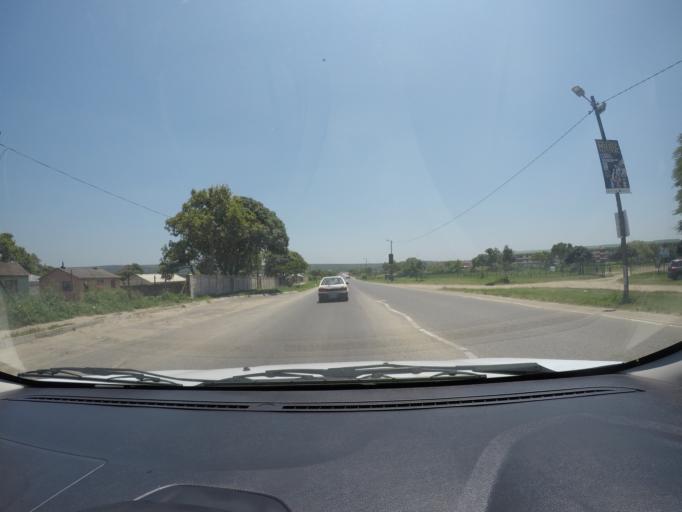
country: ZA
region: KwaZulu-Natal
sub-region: uThungulu District Municipality
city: eSikhawini
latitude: -28.8793
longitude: 31.9026
